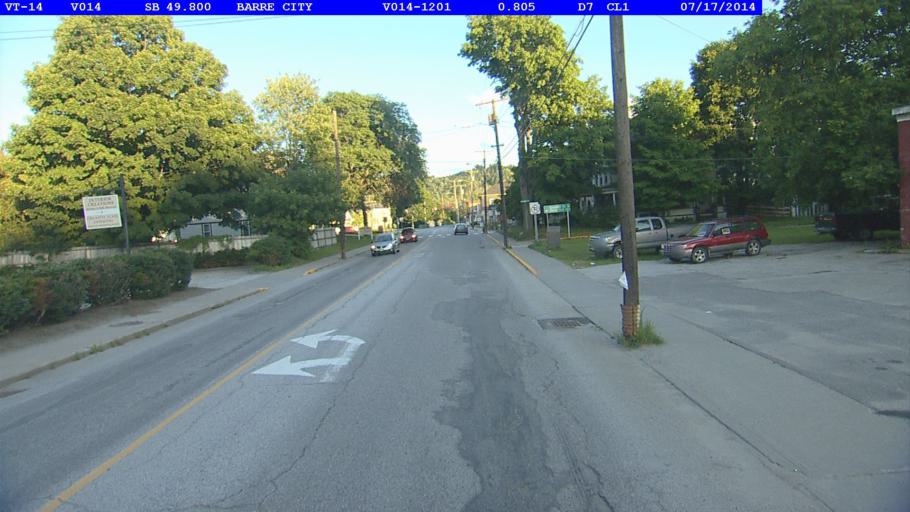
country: US
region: Vermont
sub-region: Washington County
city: Barre
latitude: 44.1920
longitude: -72.4999
